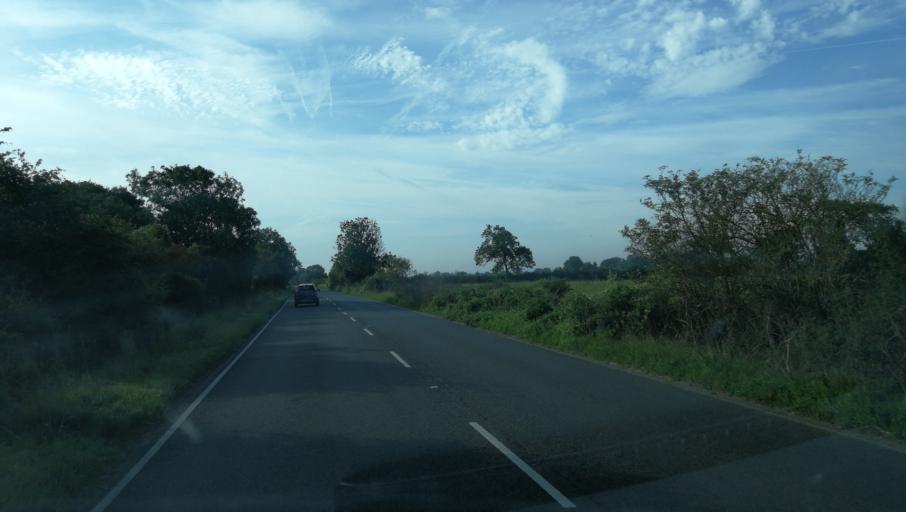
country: GB
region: England
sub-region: Oxfordshire
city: Woodstock
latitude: 51.8673
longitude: -1.3270
